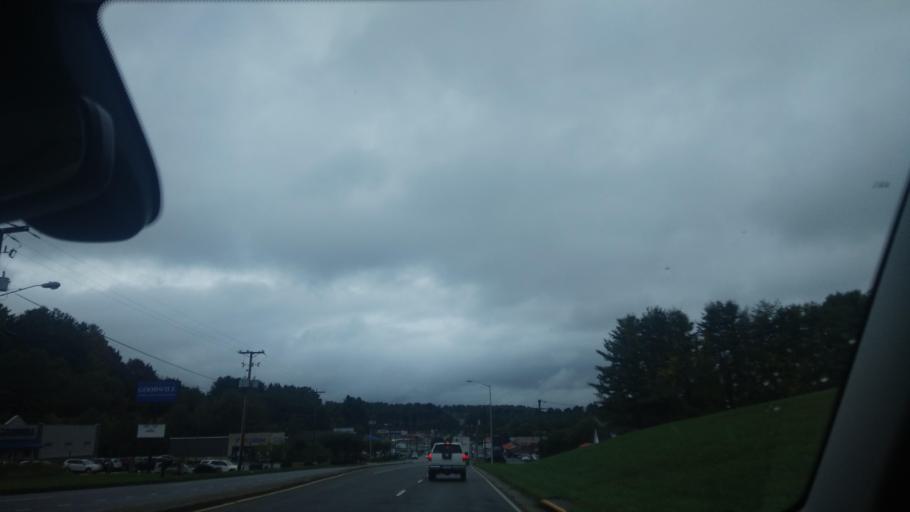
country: US
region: Virginia
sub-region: City of Galax
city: Galax
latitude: 36.6843
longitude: -80.8903
